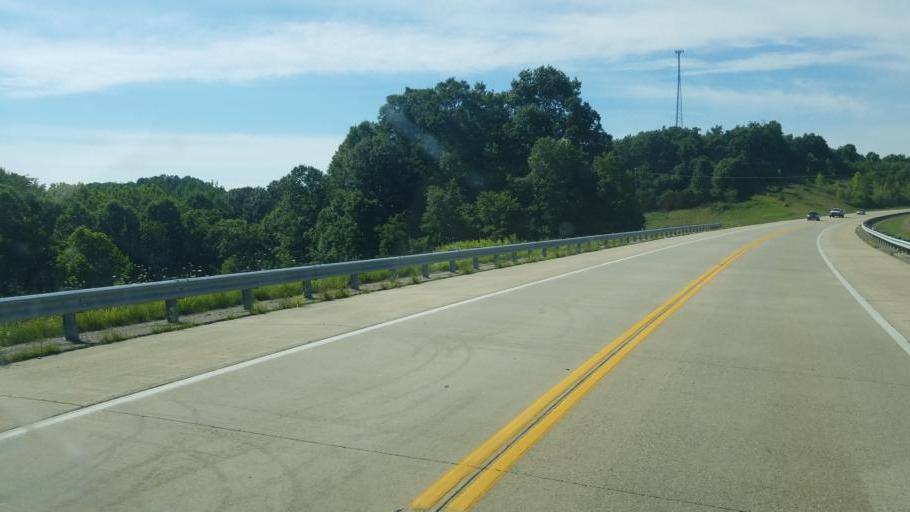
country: US
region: Ohio
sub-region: Athens County
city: Athens
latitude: 39.2142
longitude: -82.0633
